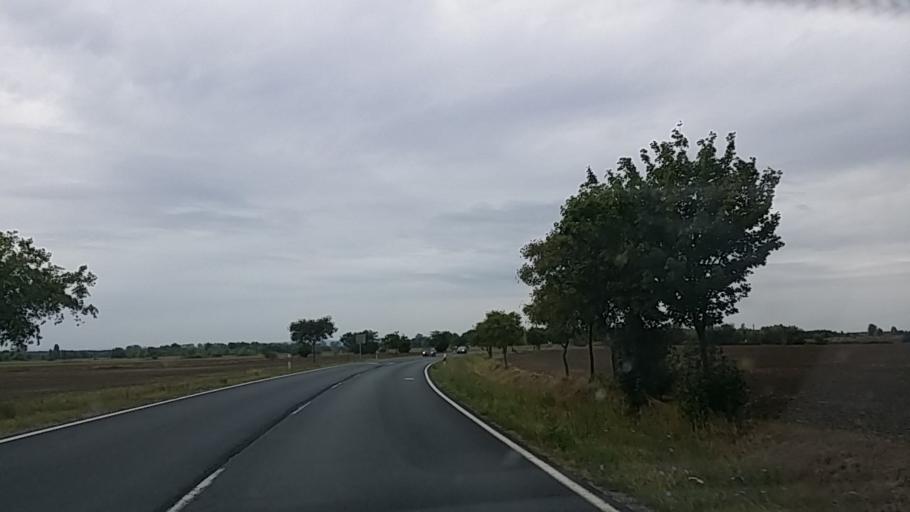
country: HU
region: Gyor-Moson-Sopron
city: Fertoszentmiklos
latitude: 47.5898
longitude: 16.8539
